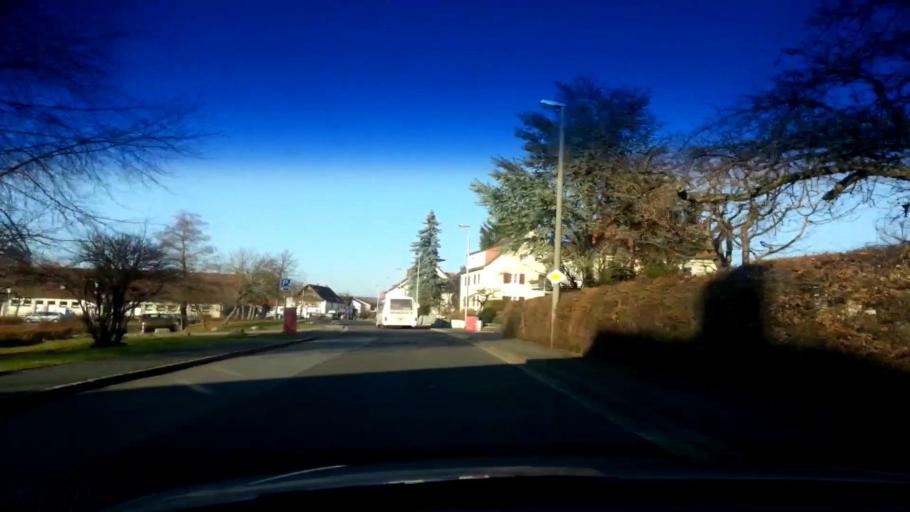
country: DE
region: Bavaria
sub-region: Upper Franconia
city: Memmelsdorf
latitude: 49.9289
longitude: 10.9560
